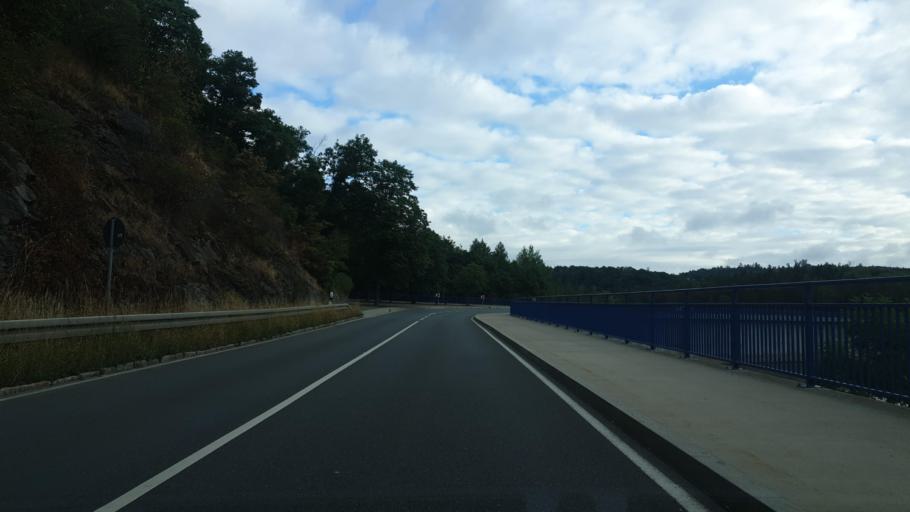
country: DE
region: Saxony
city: Pohl
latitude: 50.5489
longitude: 12.1799
